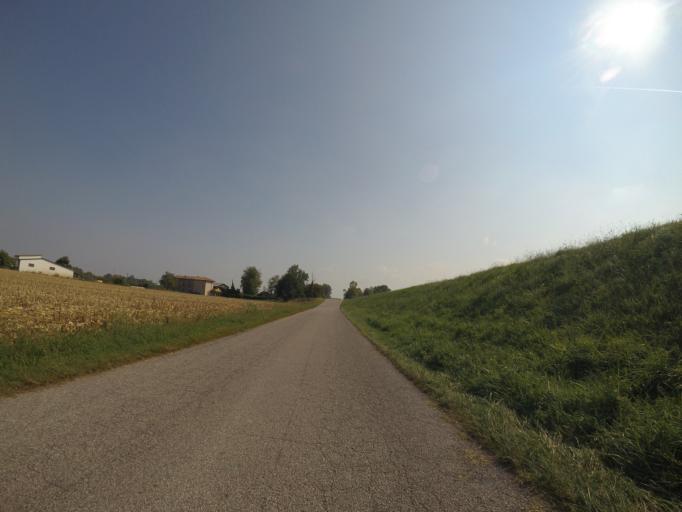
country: IT
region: Friuli Venezia Giulia
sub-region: Provincia di Udine
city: Camino al Tagliamento
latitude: 45.9065
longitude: 12.9344
